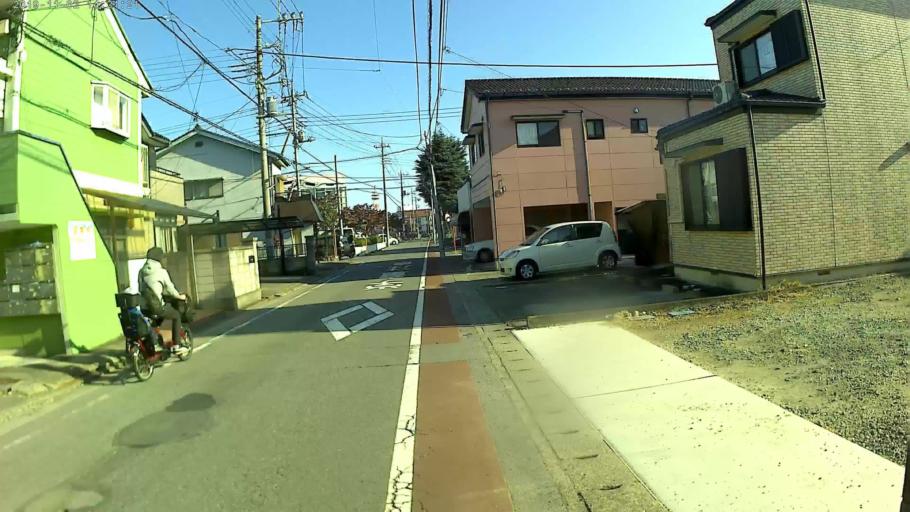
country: JP
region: Gunma
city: Takasaki
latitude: 36.3319
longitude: 138.9940
